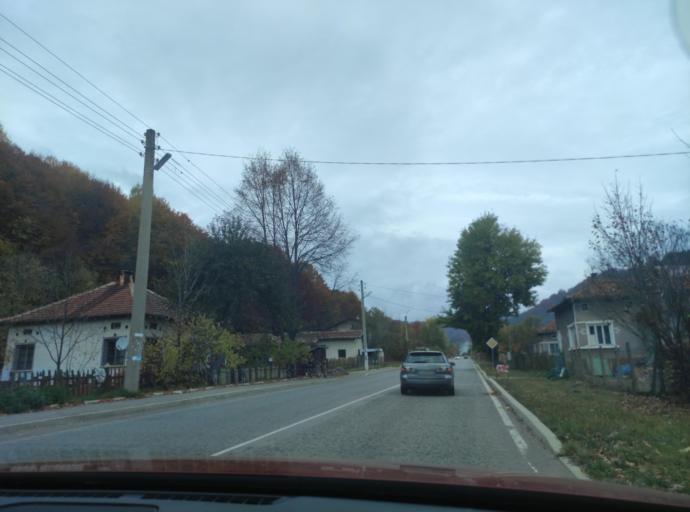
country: BG
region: Sofiya
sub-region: Obshtina Godech
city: Godech
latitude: 43.0821
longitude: 23.1042
